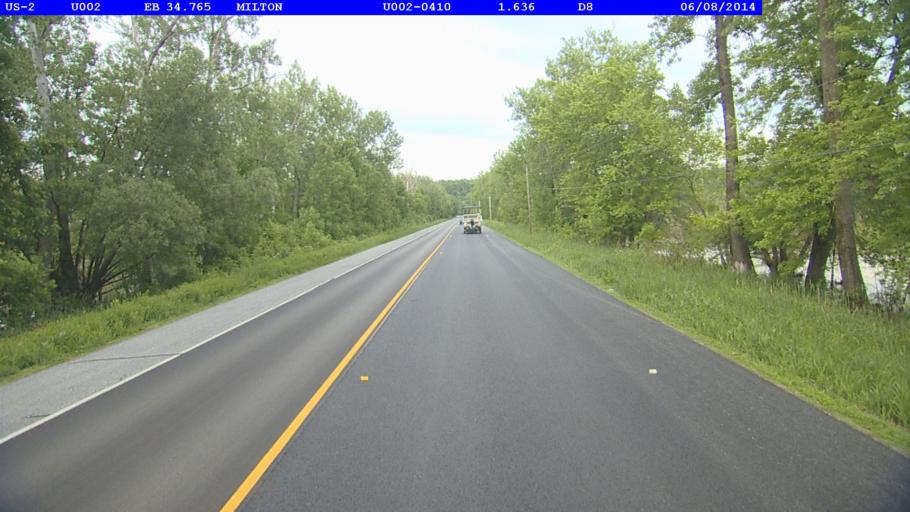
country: US
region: Vermont
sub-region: Chittenden County
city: Colchester
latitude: 44.6242
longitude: -73.2248
